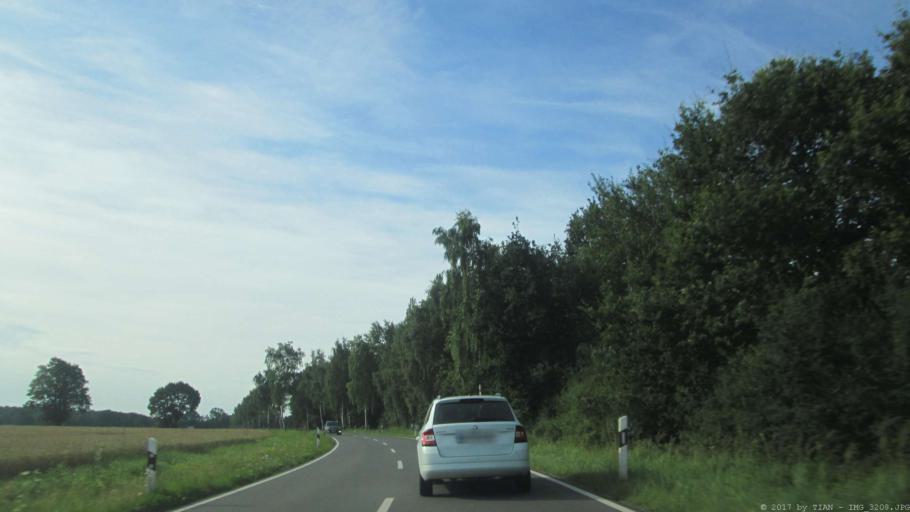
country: DE
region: Lower Saxony
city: Tiddische
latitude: 52.4940
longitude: 10.8014
